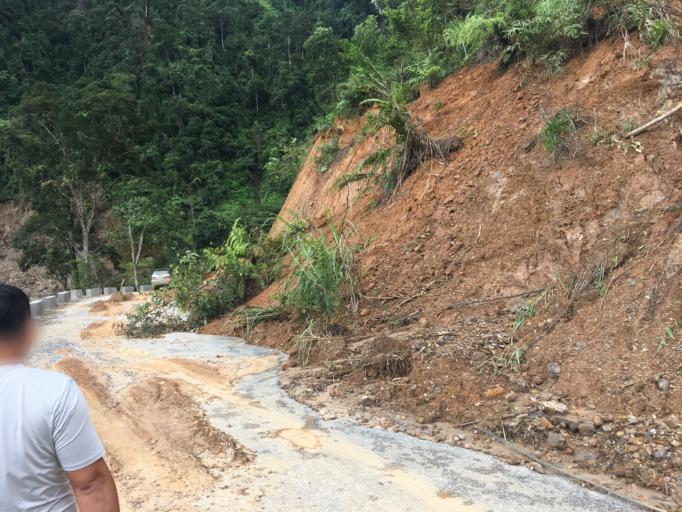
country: VN
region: Ha Giang
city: Thi Tran Tam Son
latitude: 22.9815
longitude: 105.0586
